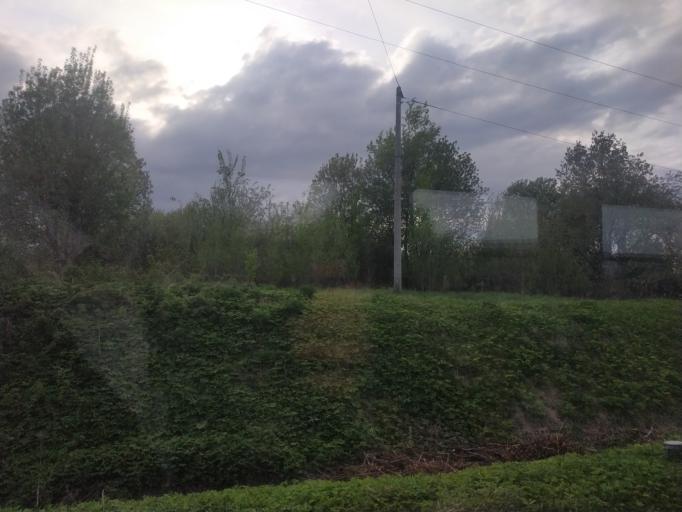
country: RU
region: Smolensk
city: Ugra
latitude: 54.7720
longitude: 34.3428
